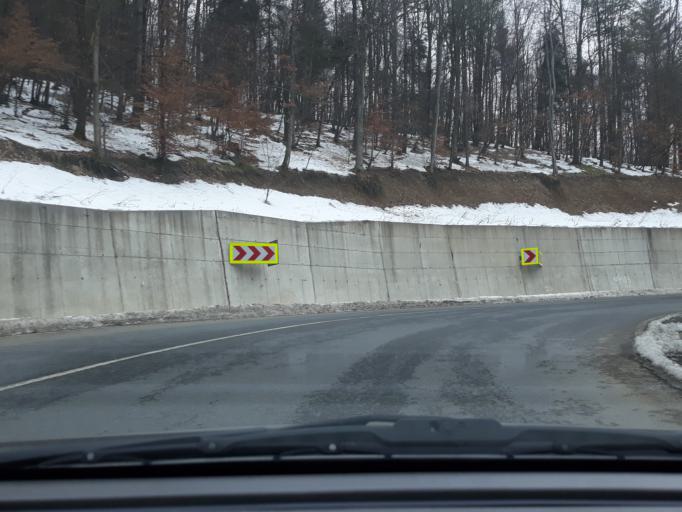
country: RO
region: Bihor
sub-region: Oras Alesd
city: Padurea Neagra
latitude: 47.1286
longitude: 22.4244
